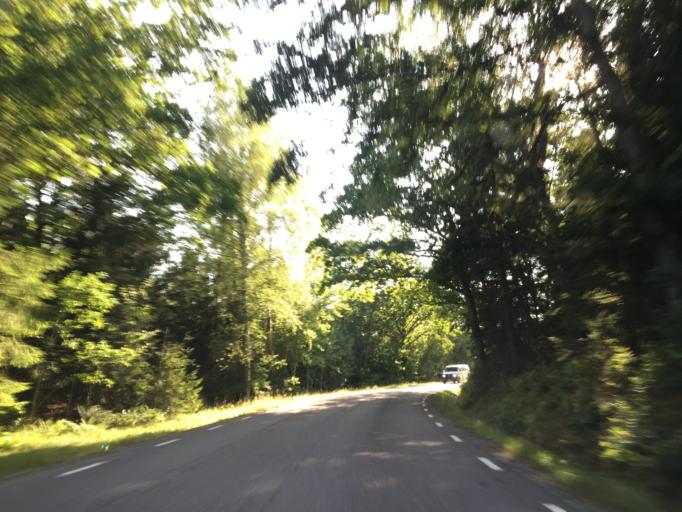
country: SE
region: Vaestra Goetaland
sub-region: Trollhattan
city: Sjuntorp
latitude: 58.2484
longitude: 12.2018
